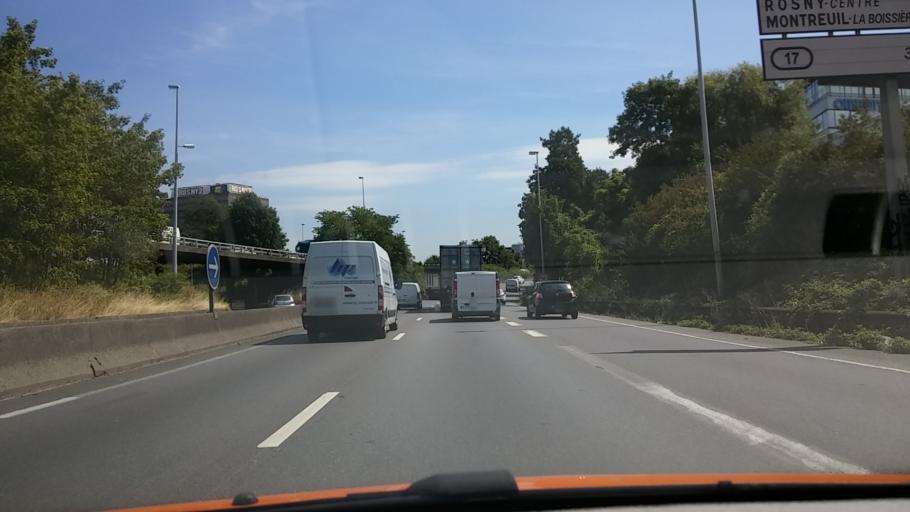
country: FR
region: Ile-de-France
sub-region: Departement de Seine-Saint-Denis
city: Noisy-le-Sec
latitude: 48.8816
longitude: 2.4735
